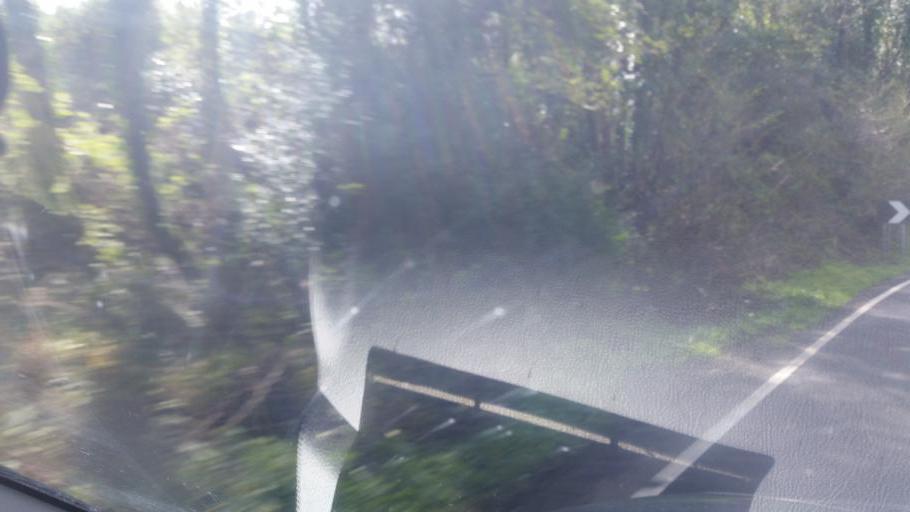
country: GB
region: Northern Ireland
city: Irvinestown
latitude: 54.4731
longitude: -7.8492
